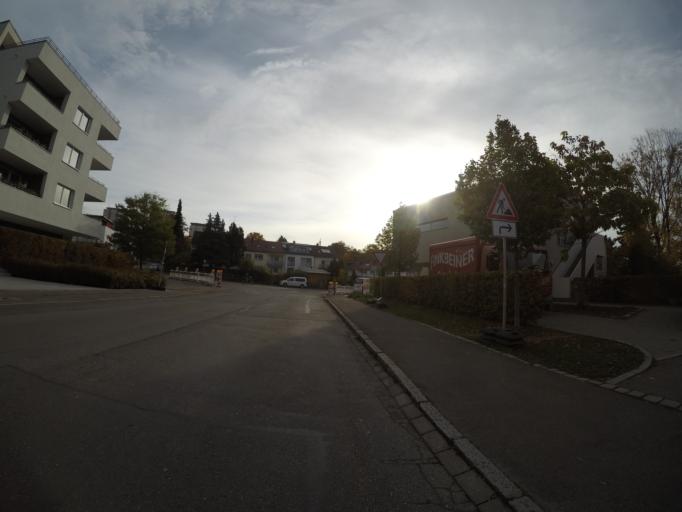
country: DE
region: Baden-Wuerttemberg
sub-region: Tuebingen Region
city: Ulm
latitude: 48.4092
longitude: 9.9554
